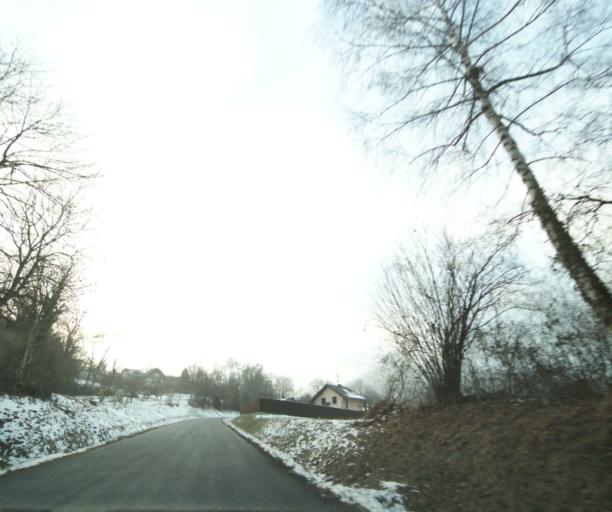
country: FR
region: Rhone-Alpes
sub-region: Departement de la Haute-Savoie
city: Vetraz-Monthoux
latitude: 46.1567
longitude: 6.2405
